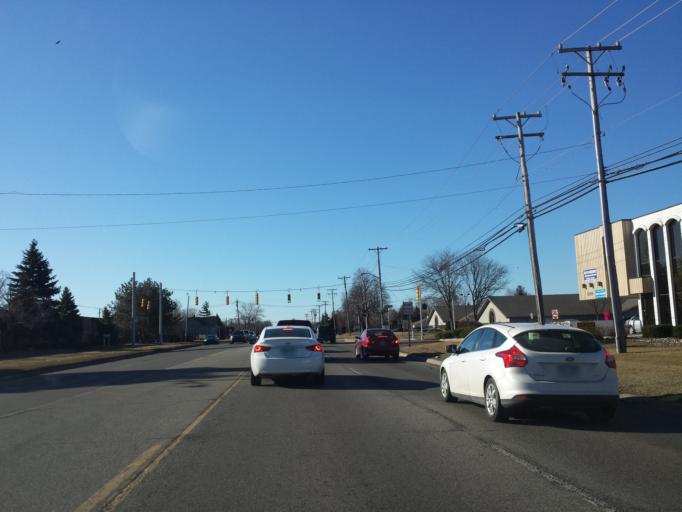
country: US
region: Michigan
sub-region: Oakland County
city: Clawson
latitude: 42.5571
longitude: -83.1474
